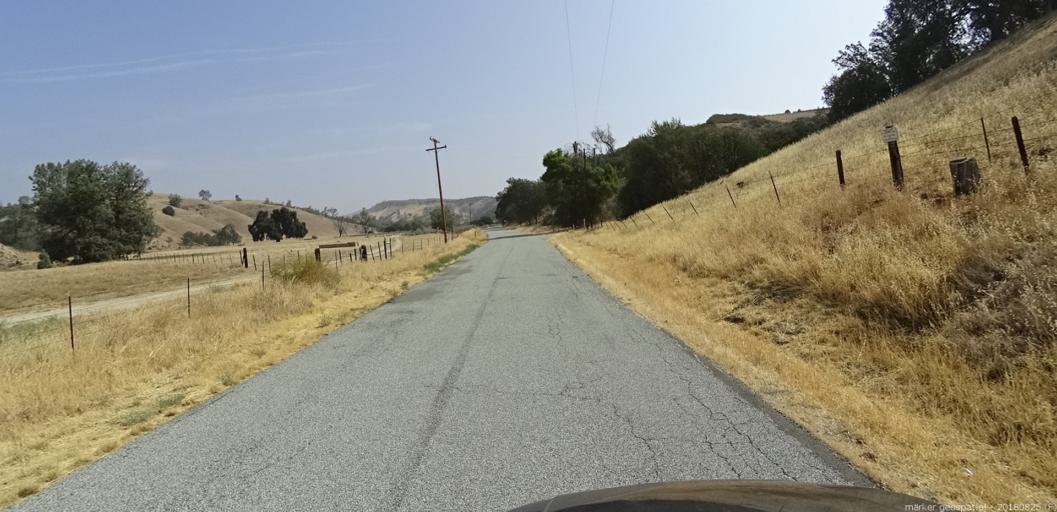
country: US
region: California
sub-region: San Luis Obispo County
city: San Miguel
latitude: 35.8535
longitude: -120.6063
